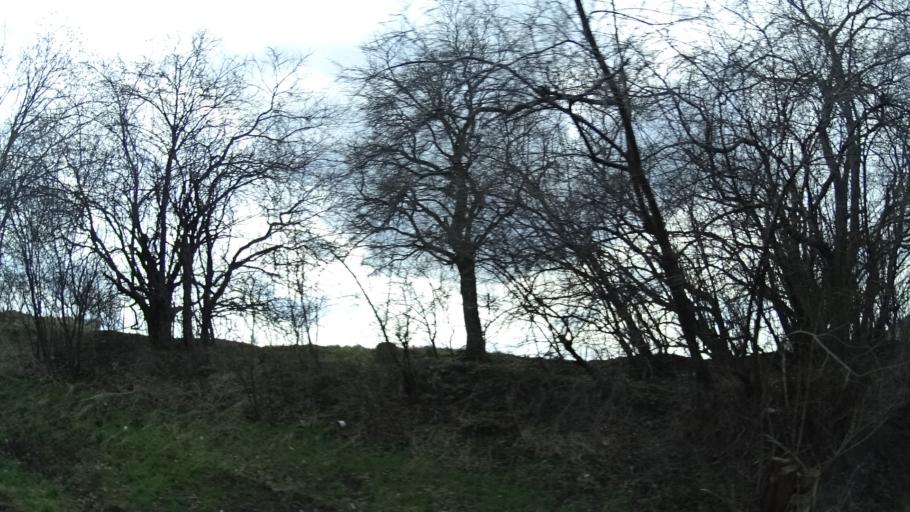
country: DE
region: Thuringia
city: Serba
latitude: 50.9515
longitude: 11.8190
